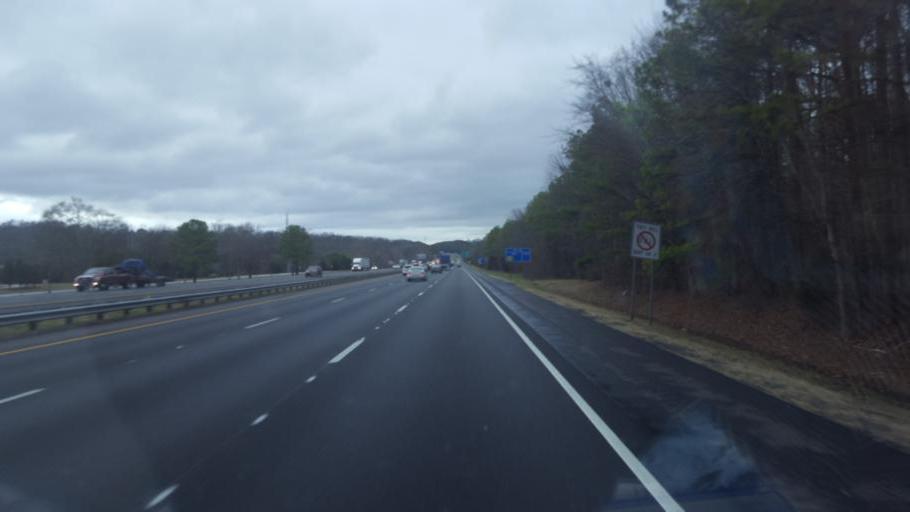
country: US
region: Georgia
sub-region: Catoosa County
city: Indian Springs
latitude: 34.9492
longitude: -85.1750
